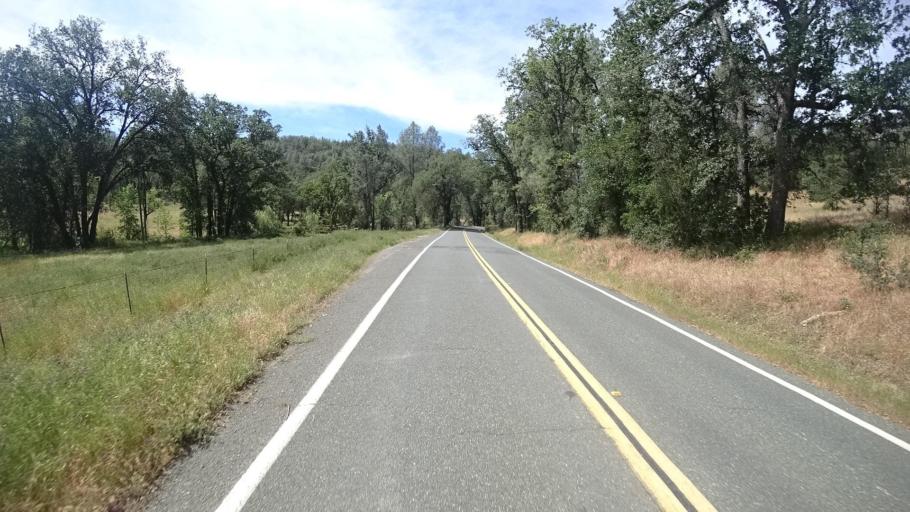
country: US
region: California
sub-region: Lake County
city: Lower Lake
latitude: 38.8994
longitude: -122.6434
